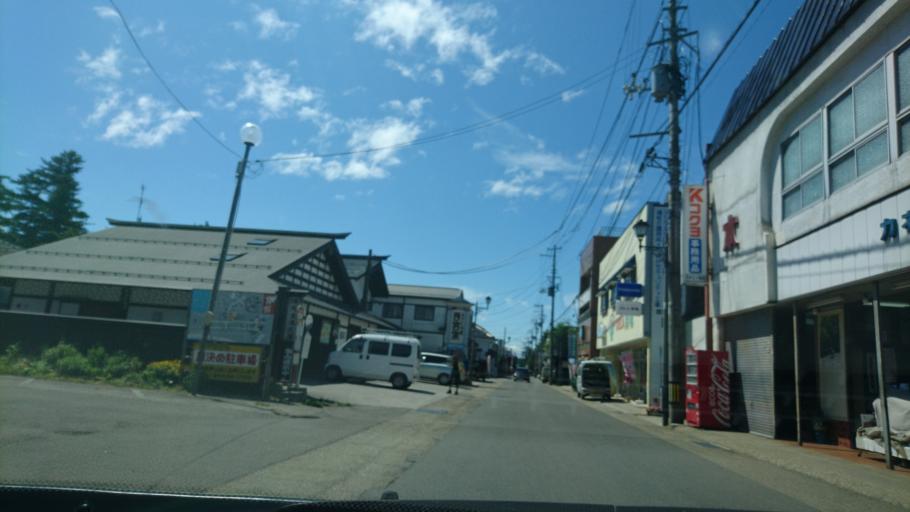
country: JP
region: Akita
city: Kakunodatemachi
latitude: 39.5934
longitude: 140.5639
